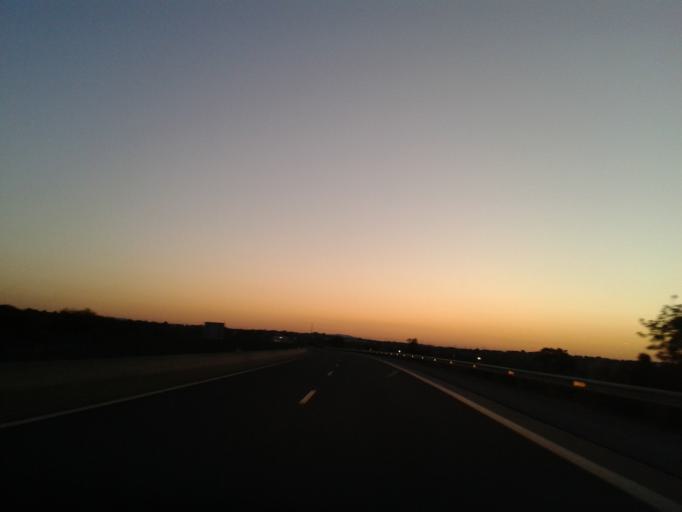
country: PT
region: Faro
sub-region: Albufeira
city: Guia
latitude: 37.1366
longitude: -8.2950
